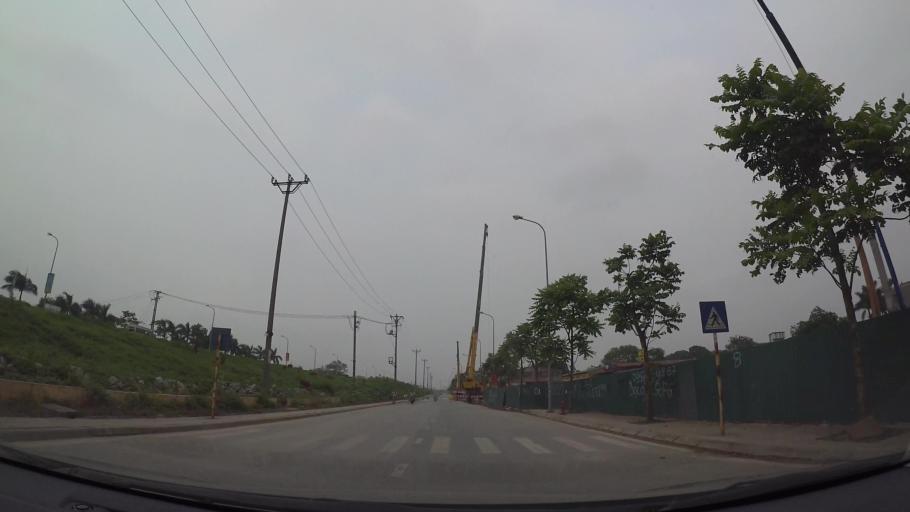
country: VN
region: Ha Noi
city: Hoan Kiem
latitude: 21.0712
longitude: 105.8842
